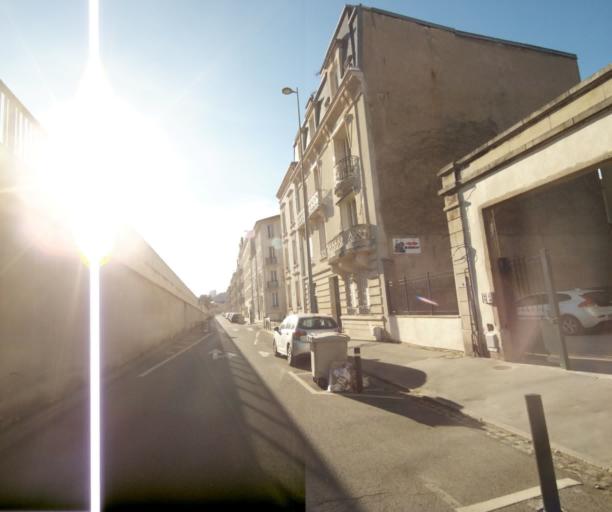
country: FR
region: Lorraine
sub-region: Departement de Meurthe-et-Moselle
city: Malzeville
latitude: 48.7004
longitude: 6.1843
